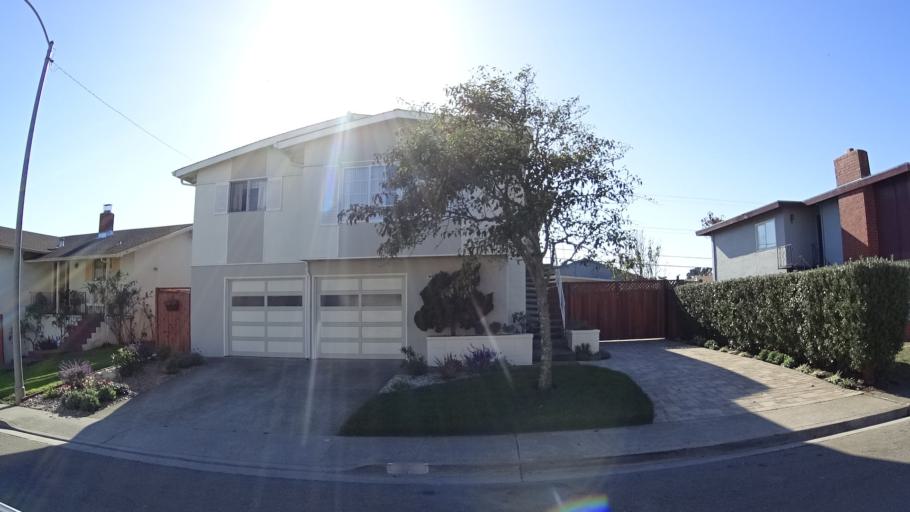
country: US
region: California
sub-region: San Mateo County
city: Pacifica
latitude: 37.6306
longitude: -122.4565
